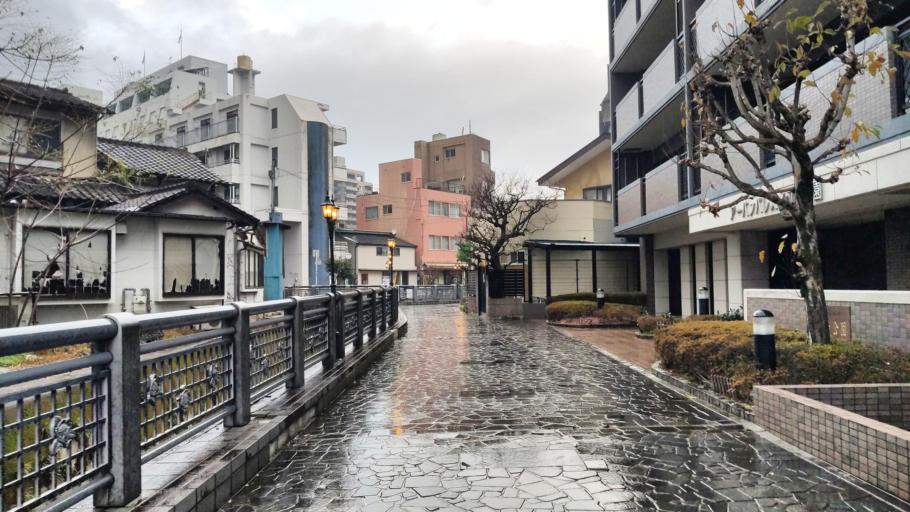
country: JP
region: Kumamoto
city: Kumamoto
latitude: 32.7906
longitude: 130.7328
